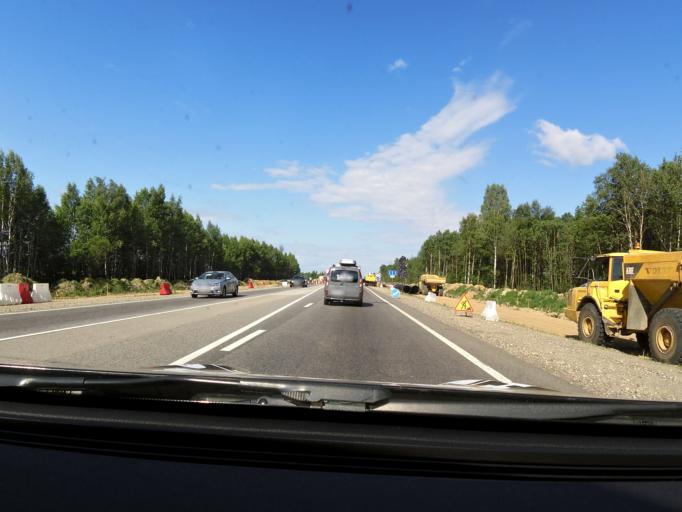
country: RU
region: Tverskaya
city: Emmaus
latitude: 56.7829
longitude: 35.9947
